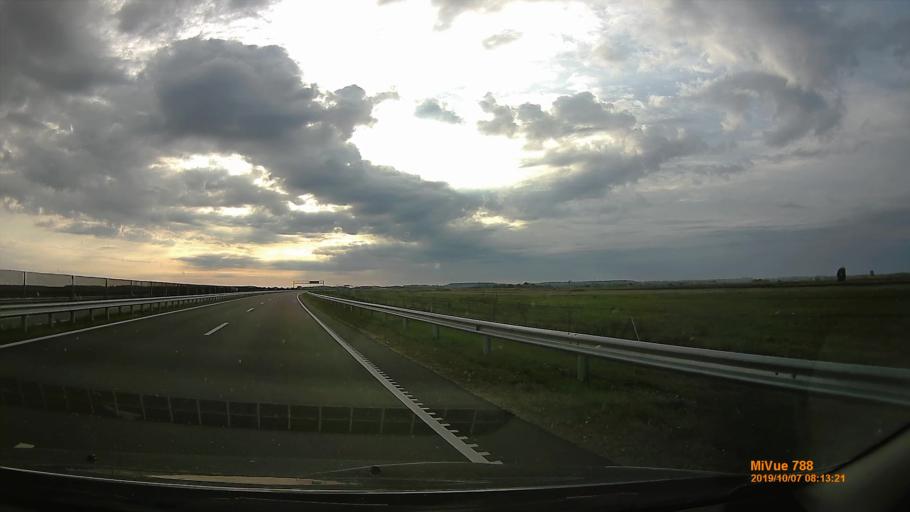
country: HU
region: Jasz-Nagykun-Szolnok
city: Cserkeszolo
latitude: 46.8806
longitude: 20.2419
